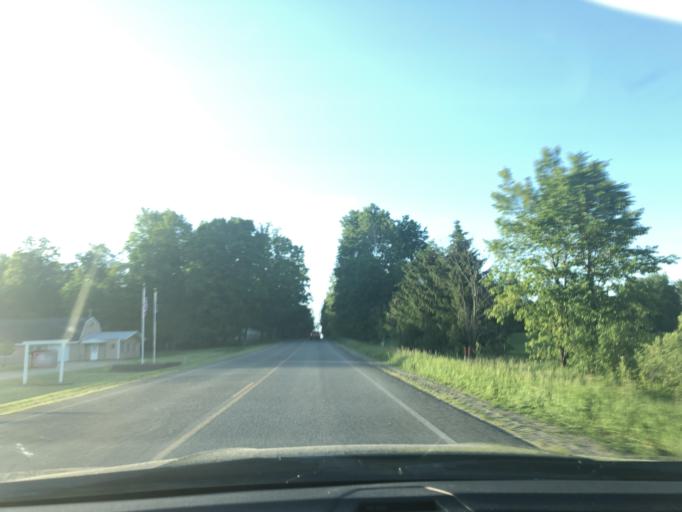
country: US
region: Michigan
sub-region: Missaukee County
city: Lake City
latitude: 44.4408
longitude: -85.0749
